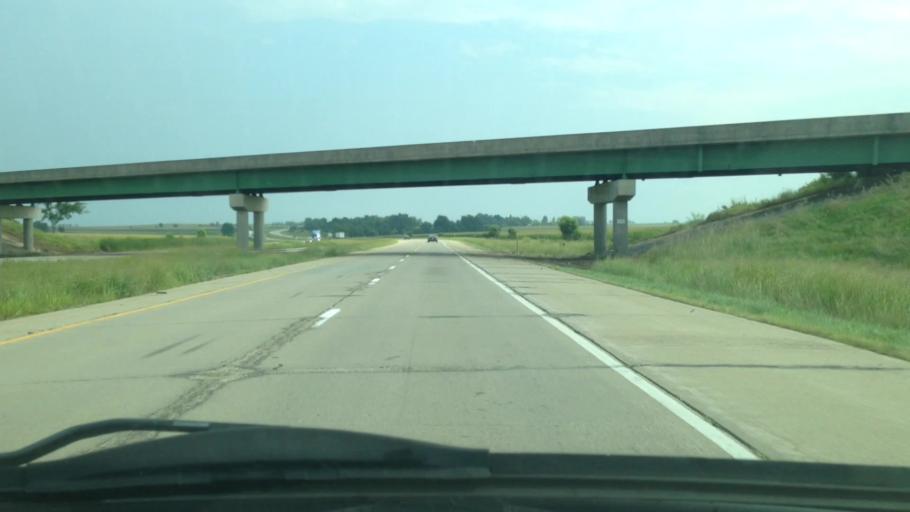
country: US
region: Iowa
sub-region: Benton County
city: Urbana
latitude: 42.2827
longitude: -91.9421
